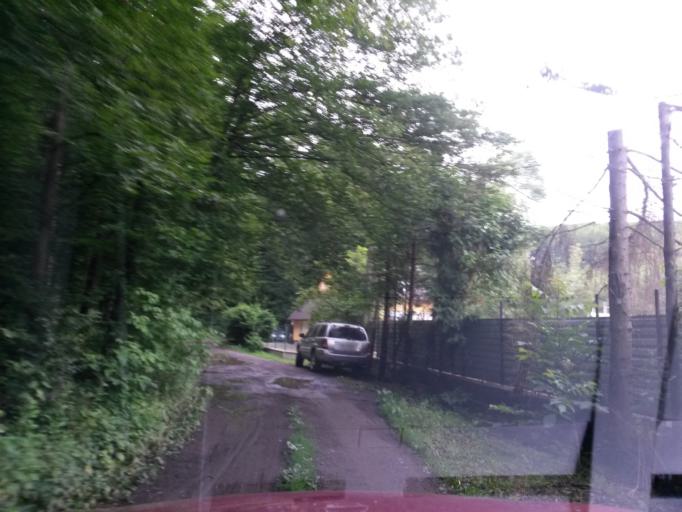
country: SK
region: Presovsky
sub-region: Okres Presov
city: Presov
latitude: 48.9874
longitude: 21.1735
